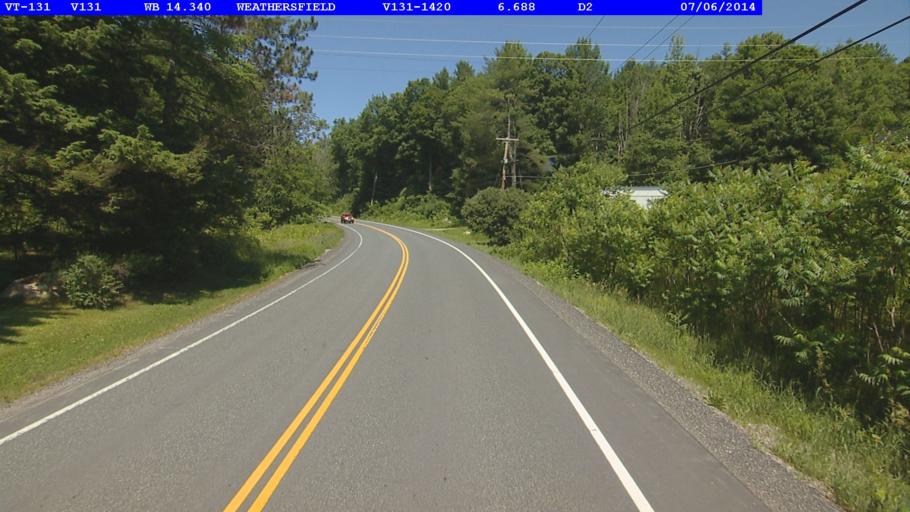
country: US
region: Vermont
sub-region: Windsor County
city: Windsor
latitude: 43.4089
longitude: -72.4407
